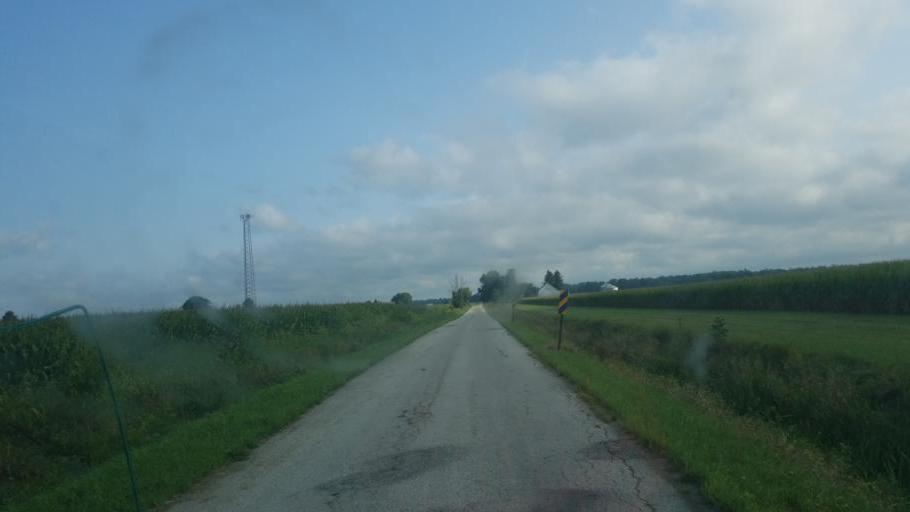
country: US
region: Ohio
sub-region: Delaware County
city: Ashley
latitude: 40.4737
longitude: -83.0077
